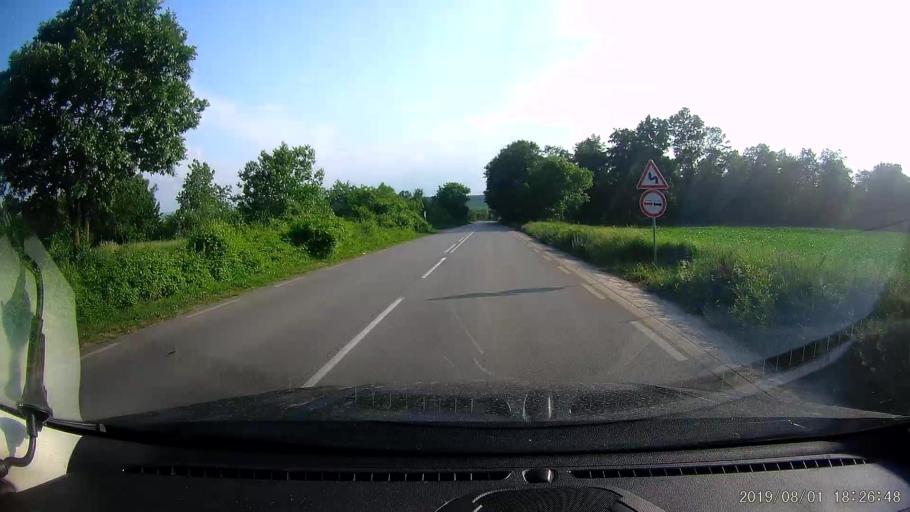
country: BG
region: Shumen
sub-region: Obshtina Venets
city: Venets
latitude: 43.5955
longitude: 26.9857
